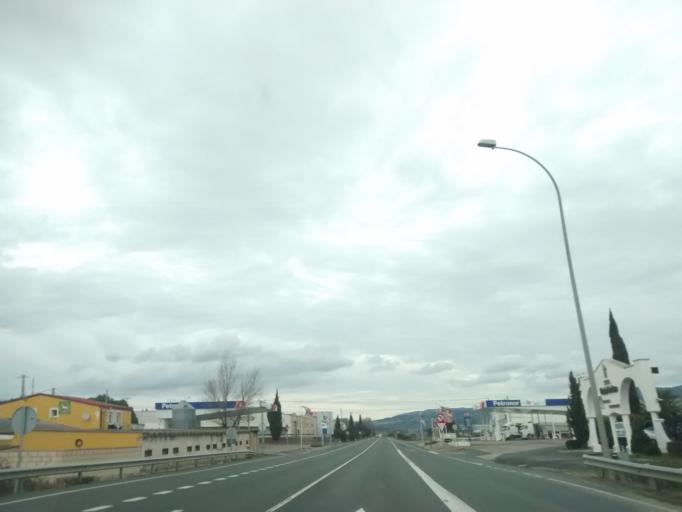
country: ES
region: La Rioja
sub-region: Provincia de La Rioja
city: Haro
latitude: 42.5652
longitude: -2.8392
